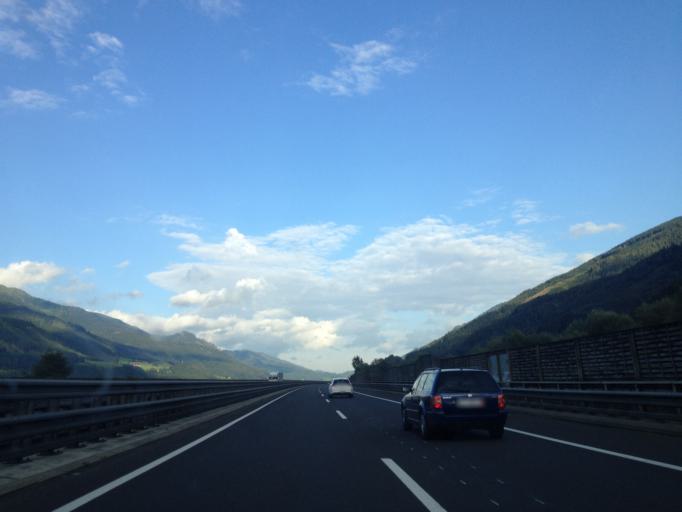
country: AT
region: Styria
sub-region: Politischer Bezirk Liezen
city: Trieben
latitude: 47.4867
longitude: 14.5235
